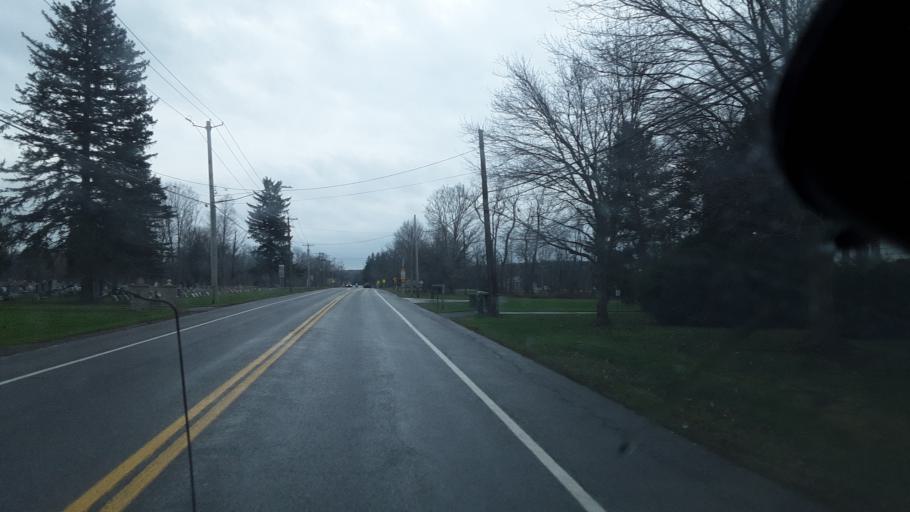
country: US
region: New York
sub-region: Erie County
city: Holland
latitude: 42.6544
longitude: -78.5522
